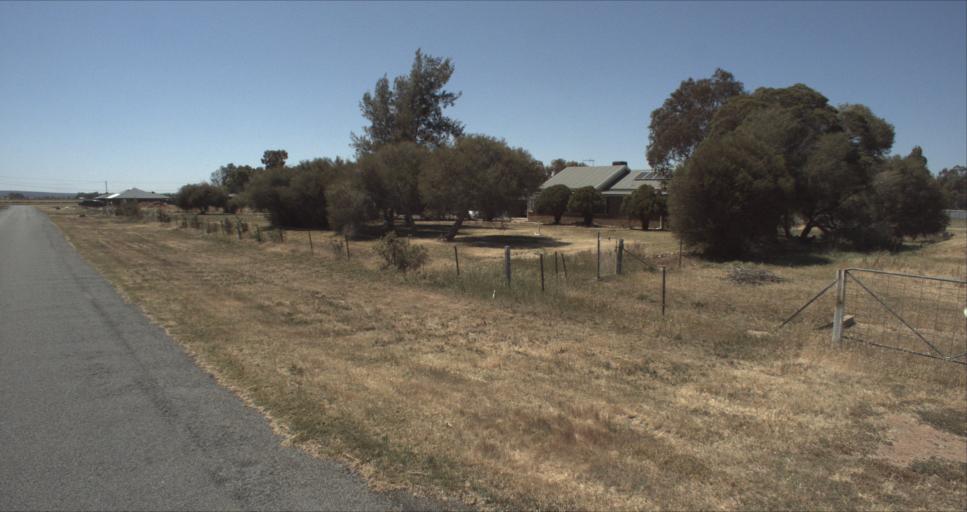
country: AU
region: New South Wales
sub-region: Leeton
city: Leeton
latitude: -34.5200
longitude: 146.4039
